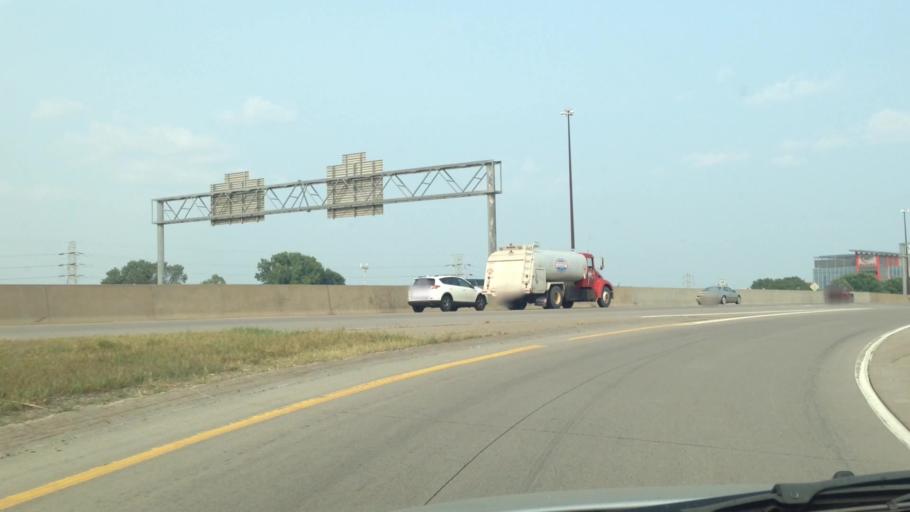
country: US
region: Minnesota
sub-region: Hennepin County
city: Edina
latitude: 44.8586
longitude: -93.3514
